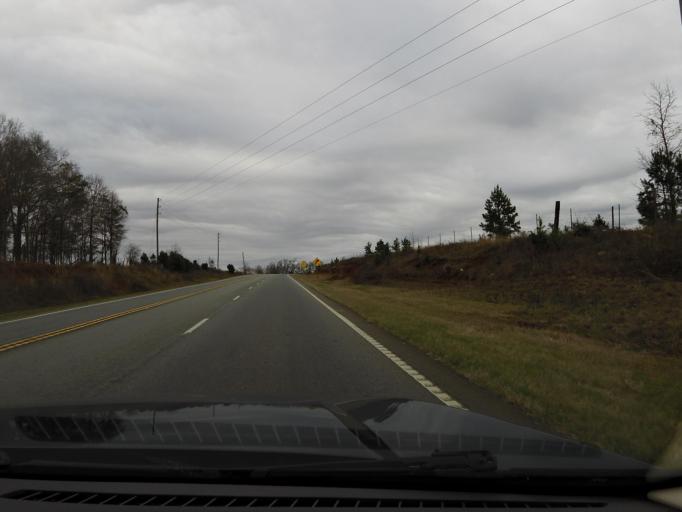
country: US
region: Georgia
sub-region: Randolph County
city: Cuthbert
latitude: 31.7775
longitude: -84.7161
